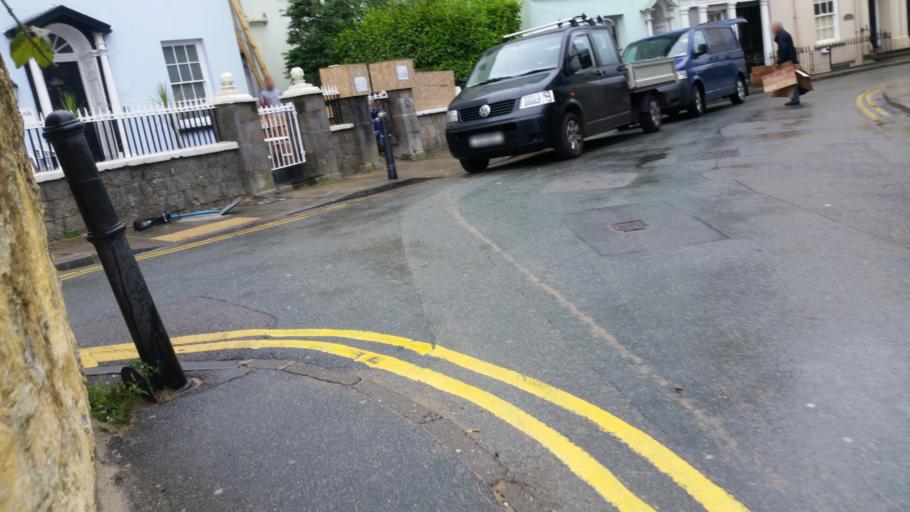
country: GB
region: Wales
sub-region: Pembrokeshire
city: Tenby
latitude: 51.6713
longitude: -4.6966
